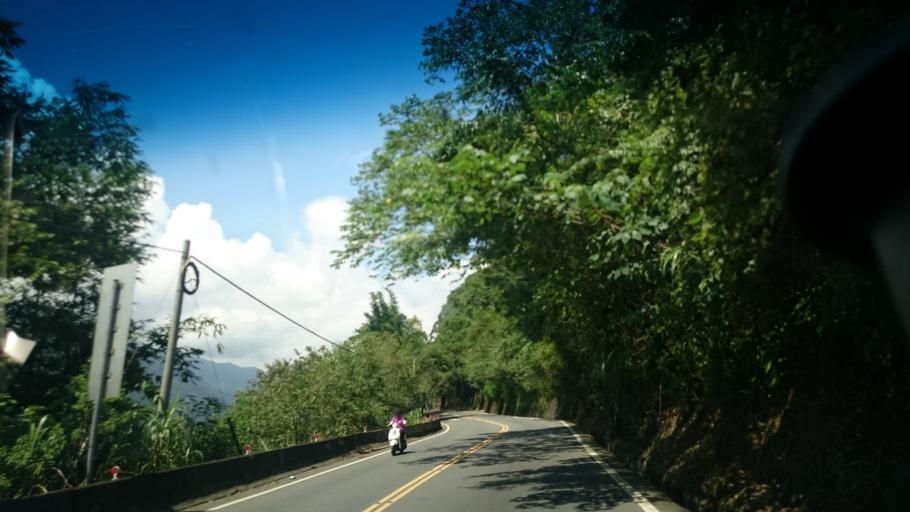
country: TW
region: Taiwan
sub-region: Nantou
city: Puli
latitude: 24.0161
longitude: 121.1286
